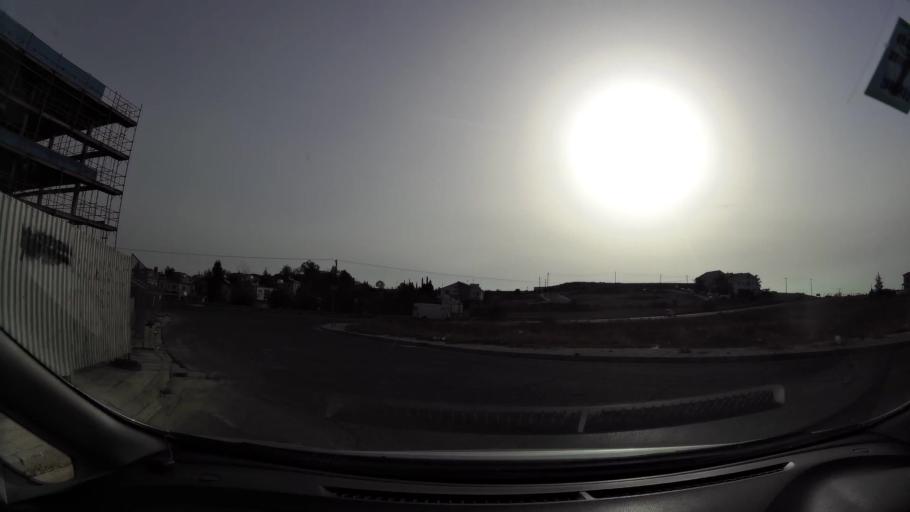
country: CY
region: Lefkosia
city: Dali
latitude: 35.0631
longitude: 33.3863
